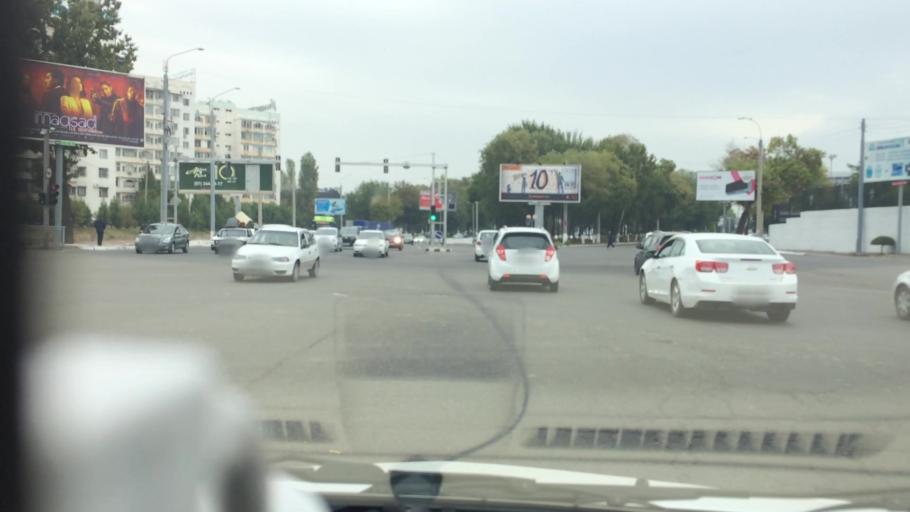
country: UZ
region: Toshkent Shahri
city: Tashkent
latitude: 41.2888
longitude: 69.2821
